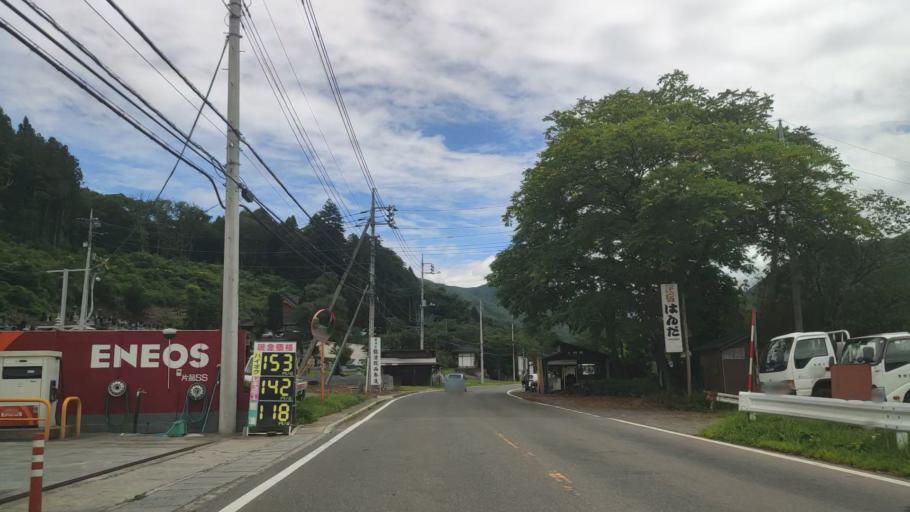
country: JP
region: Gunma
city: Numata
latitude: 36.7830
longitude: 139.2428
